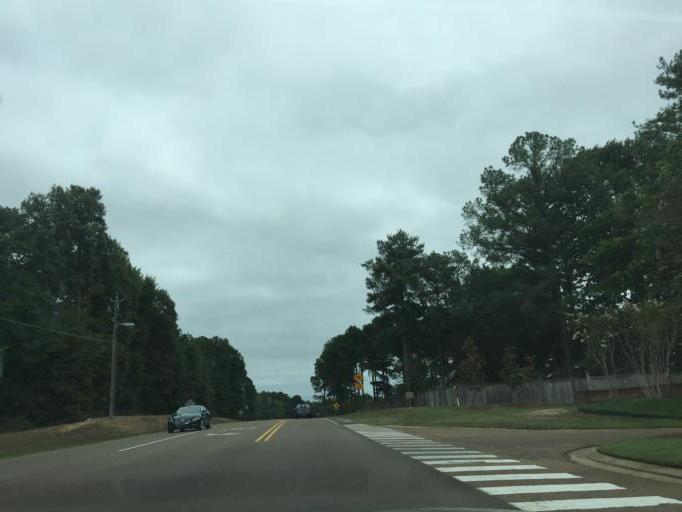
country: US
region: Mississippi
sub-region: Madison County
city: Madison
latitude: 32.4067
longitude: -90.0108
